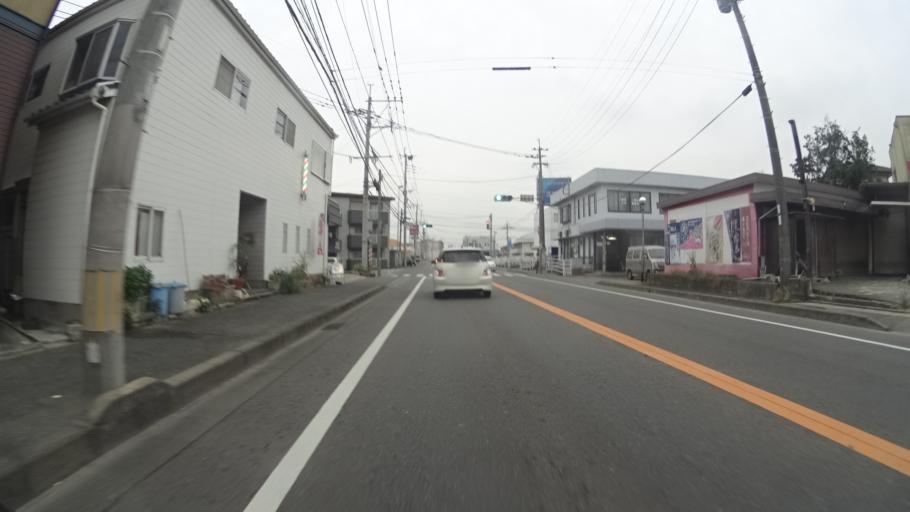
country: JP
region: Fukuoka
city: Dazaifu
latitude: 33.5174
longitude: 130.5028
